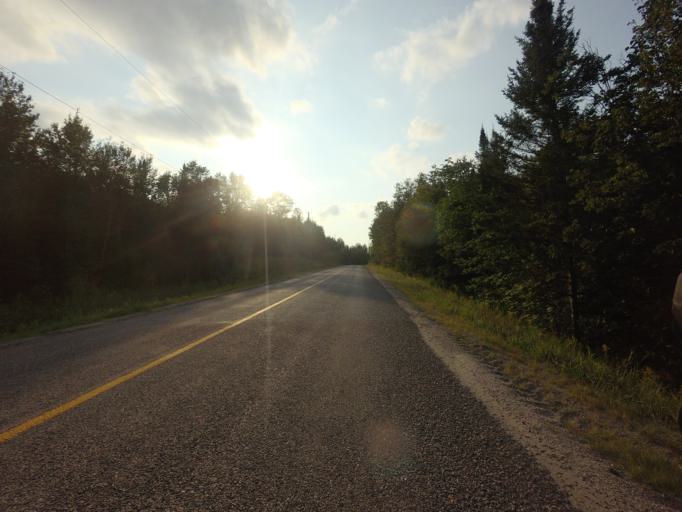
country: CA
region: Ontario
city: Perth
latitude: 44.9671
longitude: -76.7215
